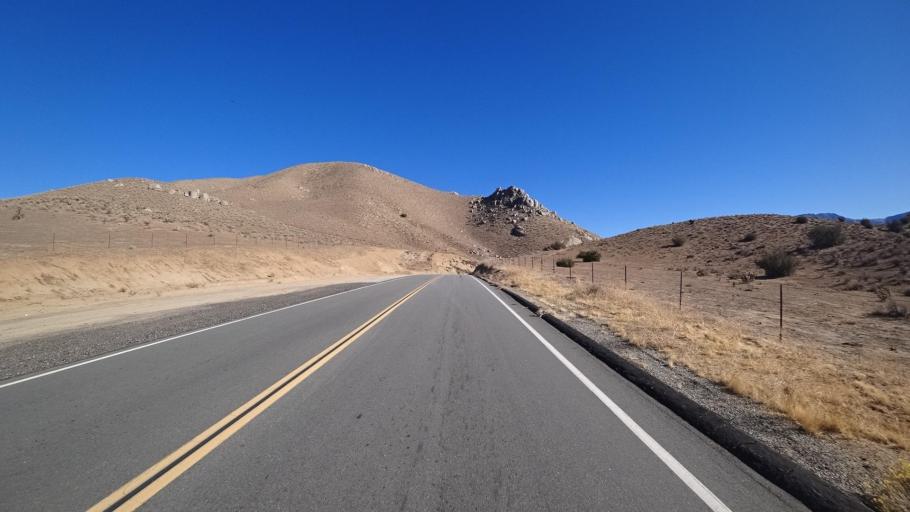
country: US
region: California
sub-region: Kern County
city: Weldon
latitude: 35.6777
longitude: -118.3591
